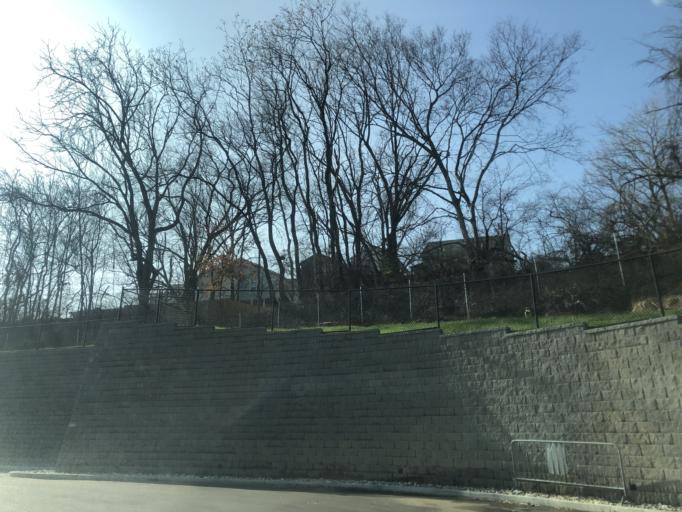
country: US
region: Tennessee
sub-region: Davidson County
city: Nashville
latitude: 36.1344
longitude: -86.7622
